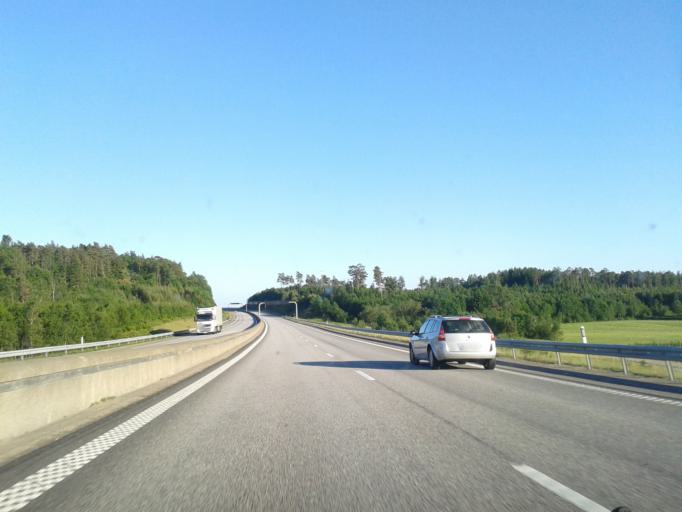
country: SE
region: Vaestra Goetaland
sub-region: Uddevalla Kommun
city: Uddevalla
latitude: 58.3370
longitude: 11.8276
